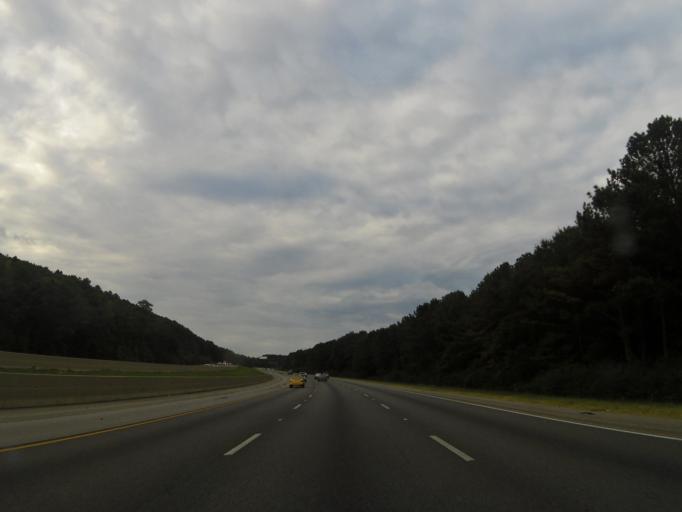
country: US
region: Alabama
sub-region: Shelby County
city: Pelham
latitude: 33.3125
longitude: -86.7865
